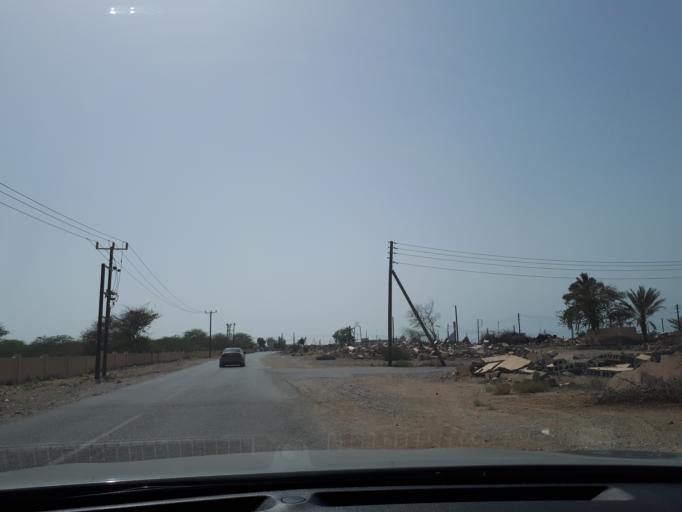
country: OM
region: Al Batinah
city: Barka'
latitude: 23.7074
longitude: 57.9079
